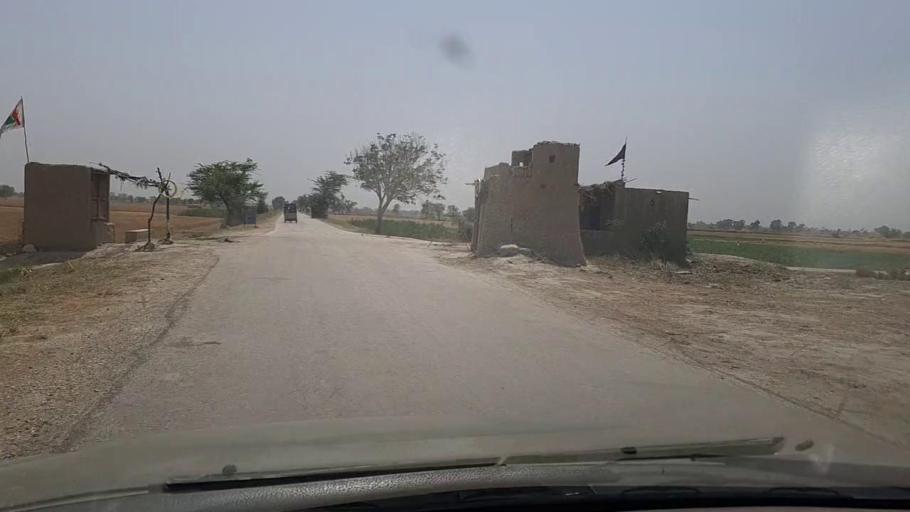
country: PK
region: Sindh
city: Miro Khan
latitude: 27.6945
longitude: 68.0584
